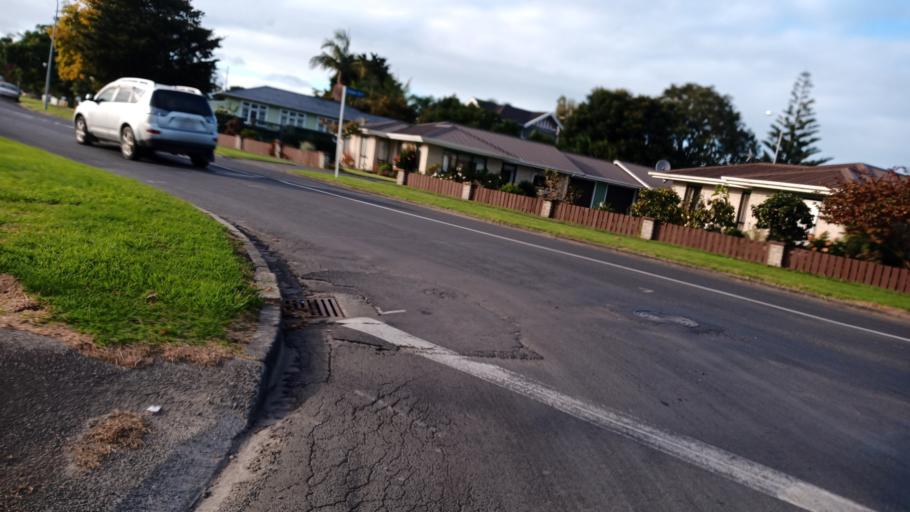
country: NZ
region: Gisborne
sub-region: Gisborne District
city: Gisborne
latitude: -38.6650
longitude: 178.0156
